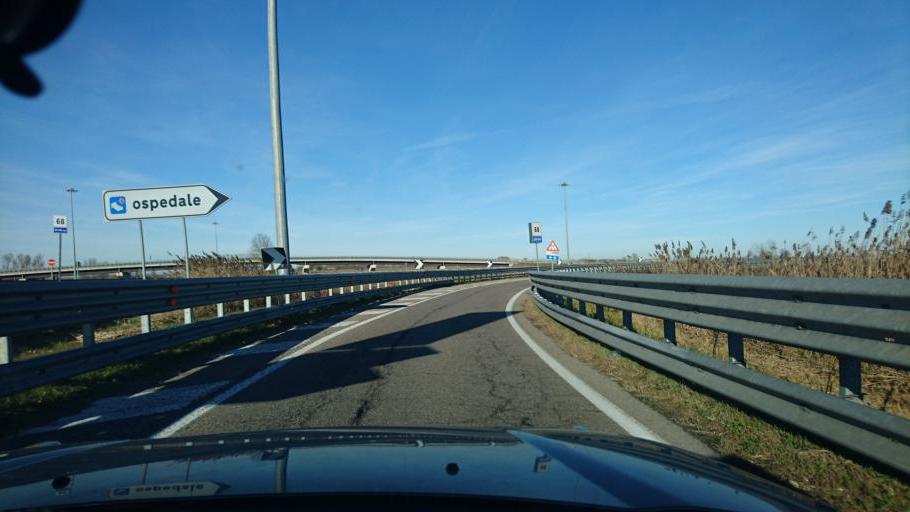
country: IT
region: Veneto
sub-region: Provincia di Rovigo
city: Bottrighe
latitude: 45.0379
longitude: 12.1005
